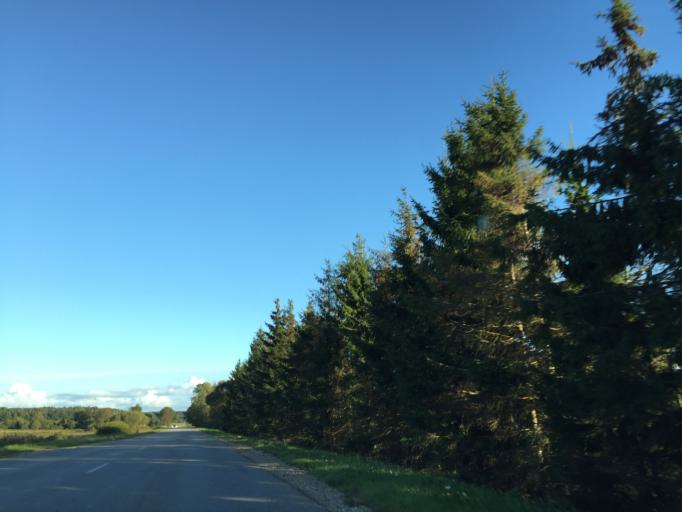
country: LV
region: Kuldigas Rajons
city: Kuldiga
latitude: 56.9352
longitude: 22.0327
